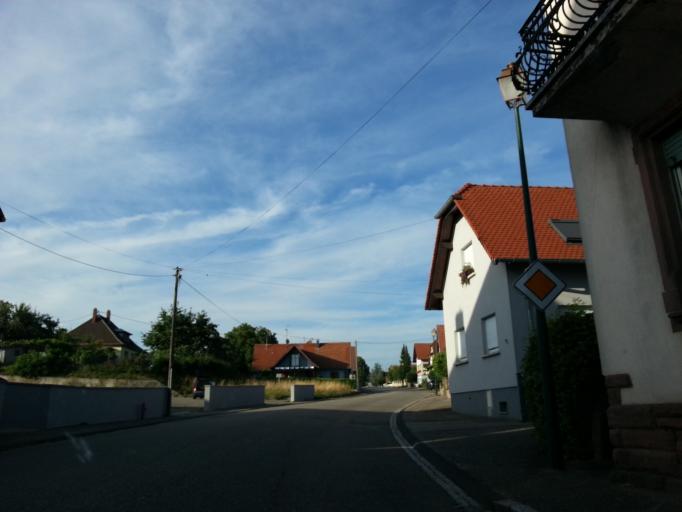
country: FR
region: Alsace
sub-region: Departement du Bas-Rhin
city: Surbourg
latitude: 48.9106
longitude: 7.8495
